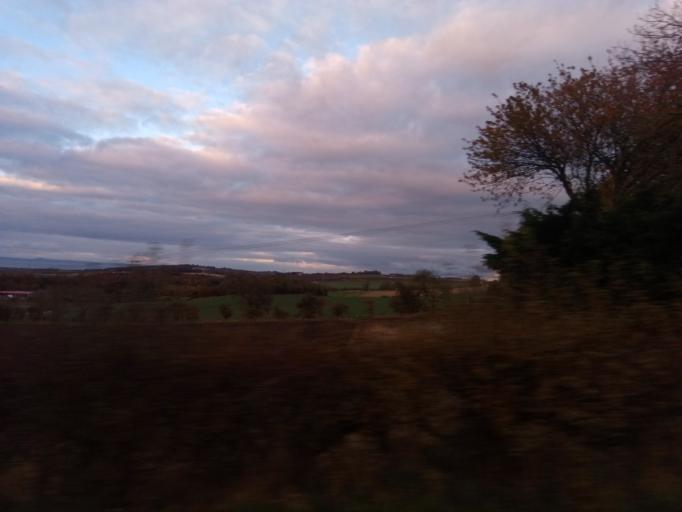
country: GB
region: Scotland
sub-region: Midlothian
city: Dalkeith
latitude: 55.8845
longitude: -3.0264
